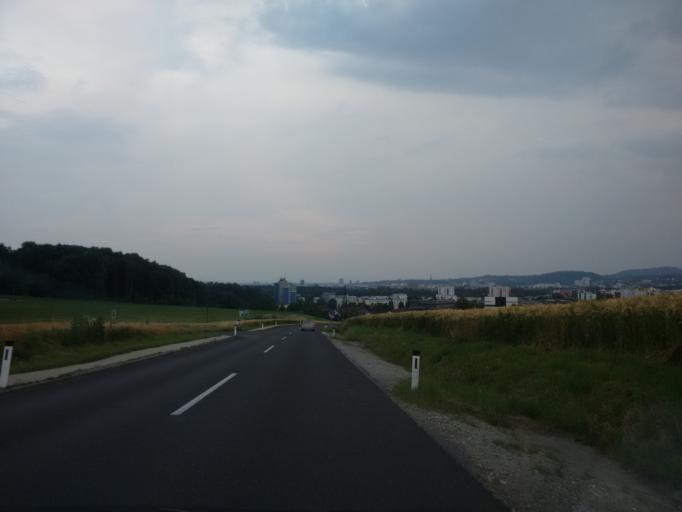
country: AT
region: Upper Austria
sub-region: Politischer Bezirk Urfahr-Umgebung
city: Altenberg bei Linz
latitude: 48.3382
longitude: 14.3275
